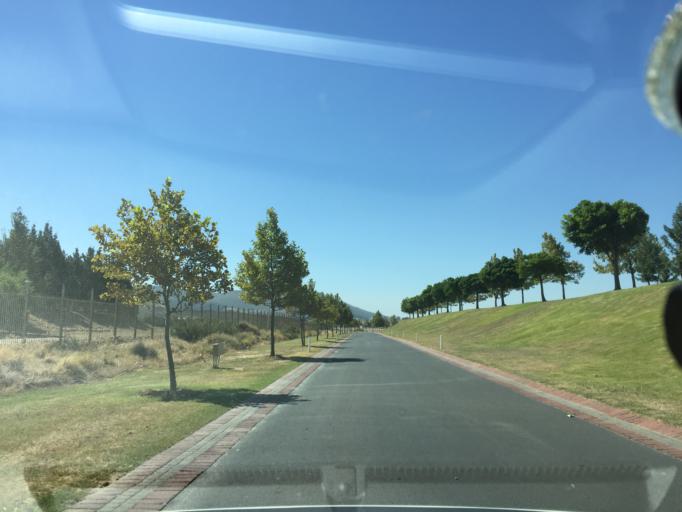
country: ZA
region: Western Cape
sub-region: Cape Winelands District Municipality
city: Paarl
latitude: -33.8076
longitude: 18.9737
